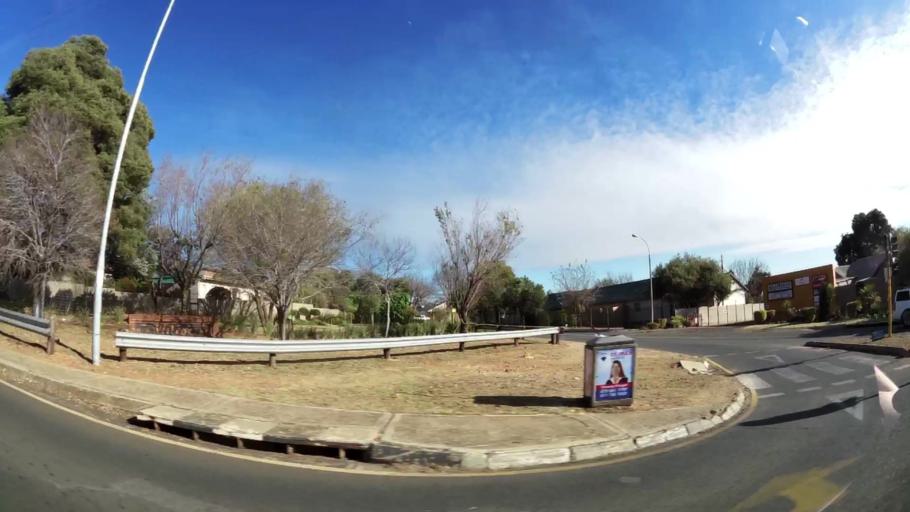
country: ZA
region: Gauteng
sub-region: City of Johannesburg Metropolitan Municipality
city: Roodepoort
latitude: -26.1222
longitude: 27.8493
